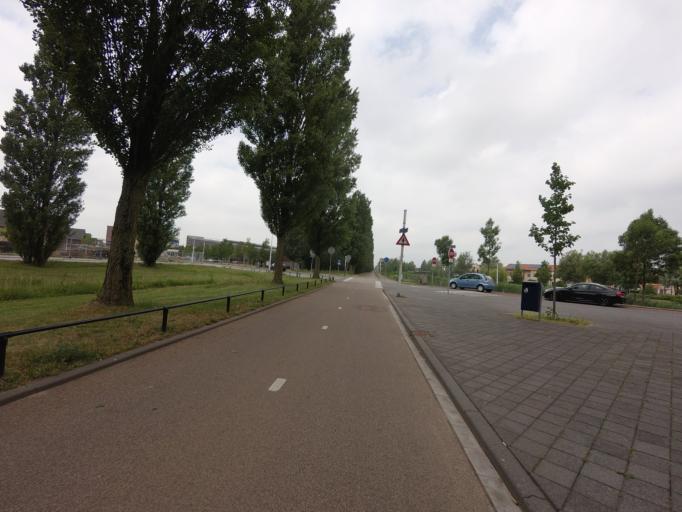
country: NL
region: Utrecht
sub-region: Stichtse Vecht
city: Maarssen
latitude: 52.1019
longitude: 5.0484
